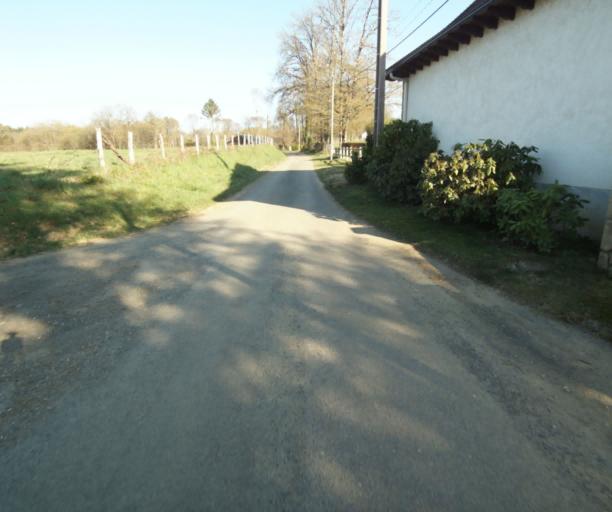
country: FR
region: Limousin
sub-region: Departement de la Correze
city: Saint-Clement
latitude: 45.3297
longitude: 1.6790
